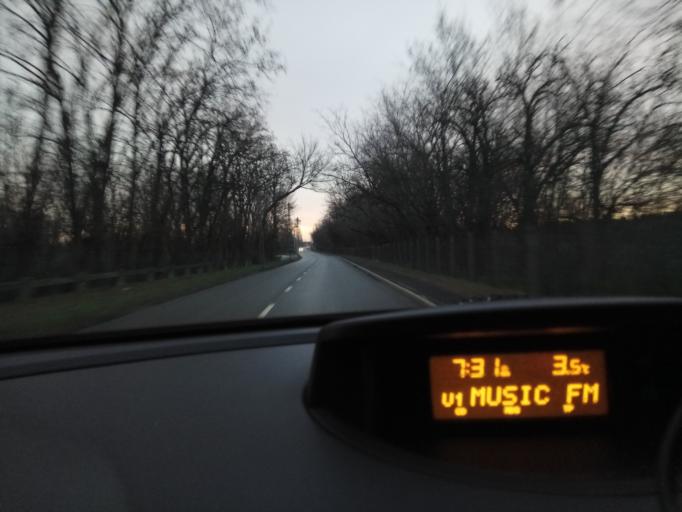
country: HU
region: Pest
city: Dunakeszi
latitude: 47.6189
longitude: 19.1338
